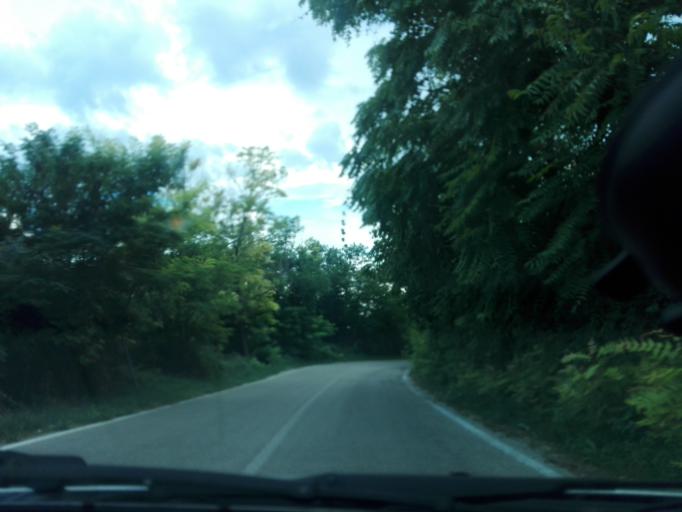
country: IT
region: Abruzzo
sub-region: Provincia di Pescara
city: Spoltore
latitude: 42.4759
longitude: 14.1369
